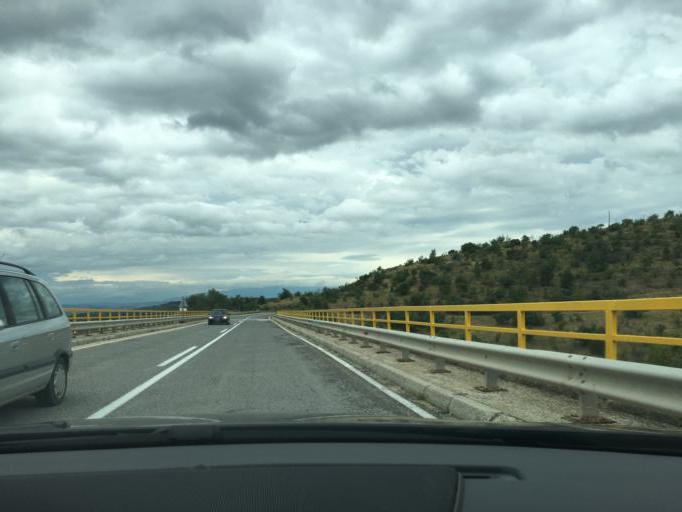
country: MK
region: Opstina Rankovce
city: Rankovce
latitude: 42.1463
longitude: 22.0068
